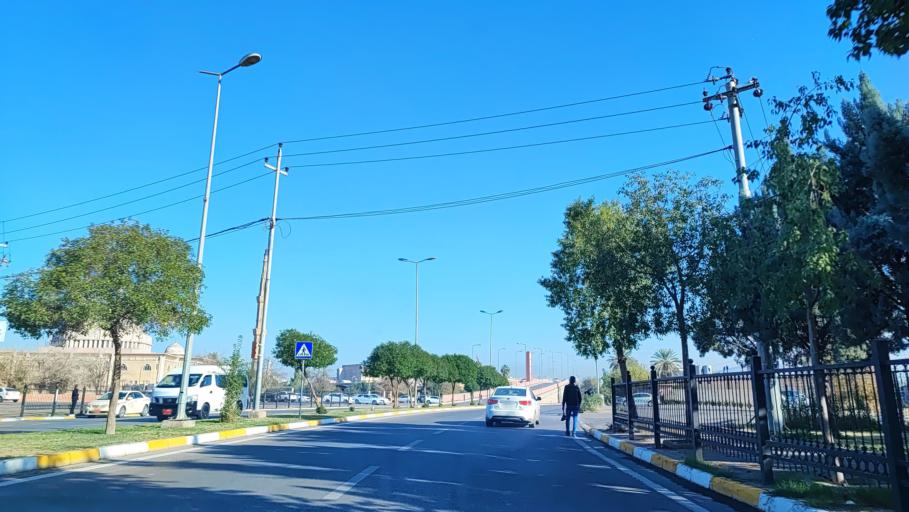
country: IQ
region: Arbil
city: Erbil
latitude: 36.1817
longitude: 44.0042
